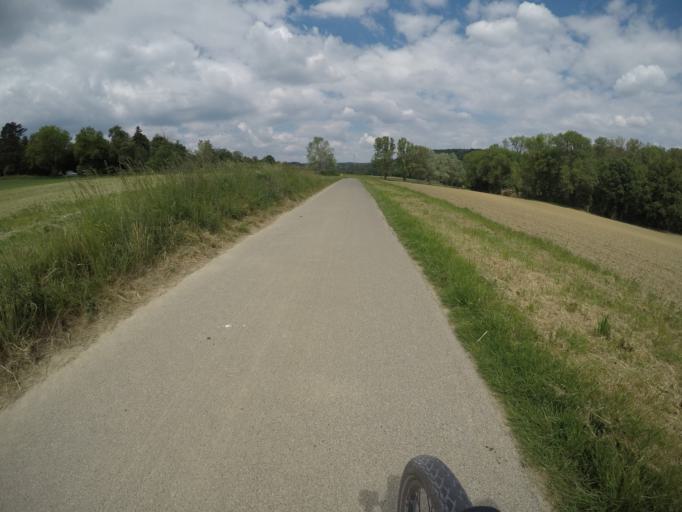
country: DE
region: Baden-Wuerttemberg
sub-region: Regierungsbezirk Stuttgart
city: Ostfildern
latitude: 48.7185
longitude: 9.2181
